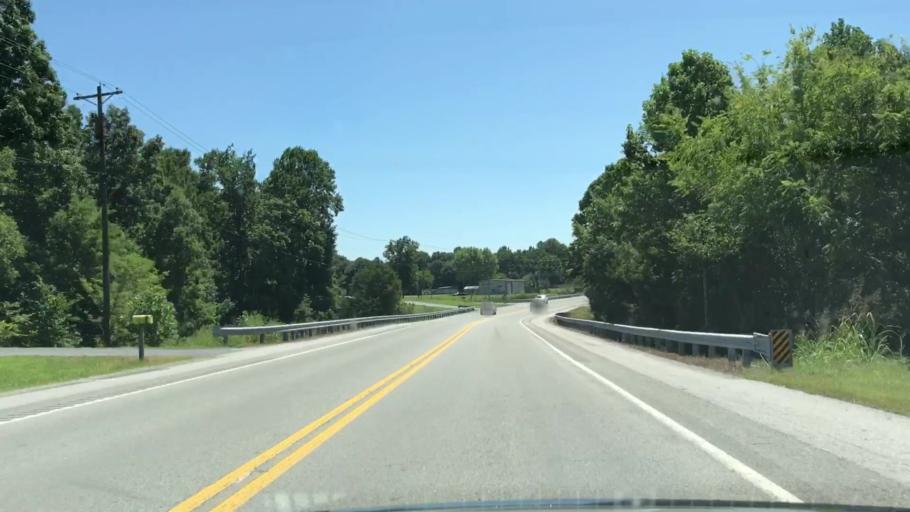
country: US
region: Tennessee
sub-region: Jackson County
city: Gainesboro
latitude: 36.2774
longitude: -85.6181
